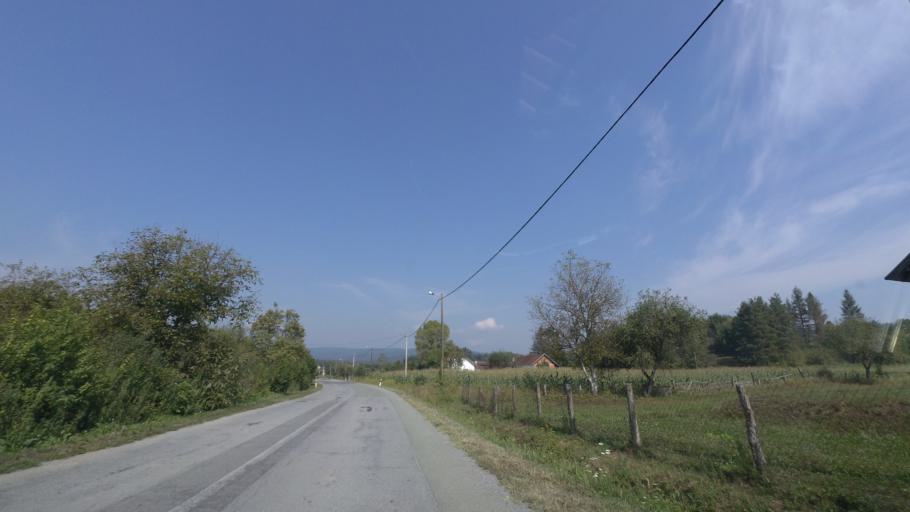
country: HR
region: Sisacko-Moslavacka
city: Dvor
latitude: 45.1071
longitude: 16.2858
